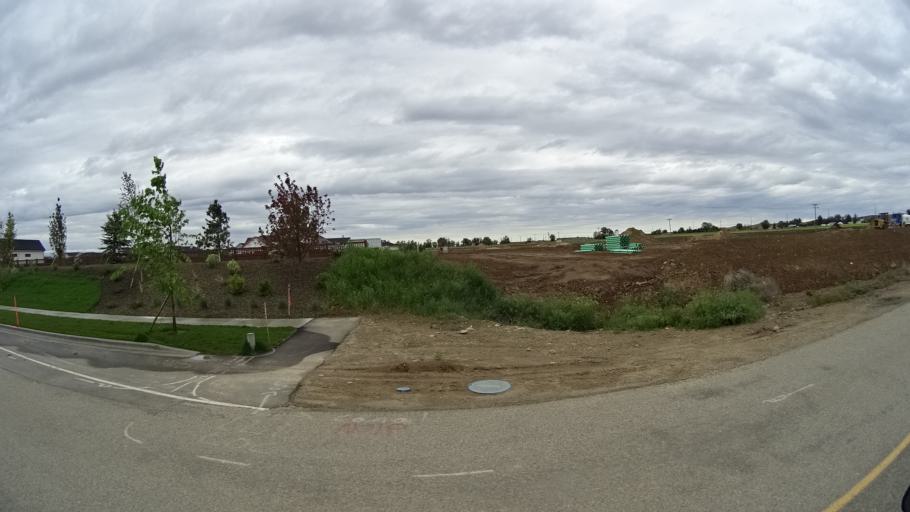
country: US
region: Idaho
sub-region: Ada County
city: Eagle
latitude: 43.7161
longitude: -116.4235
